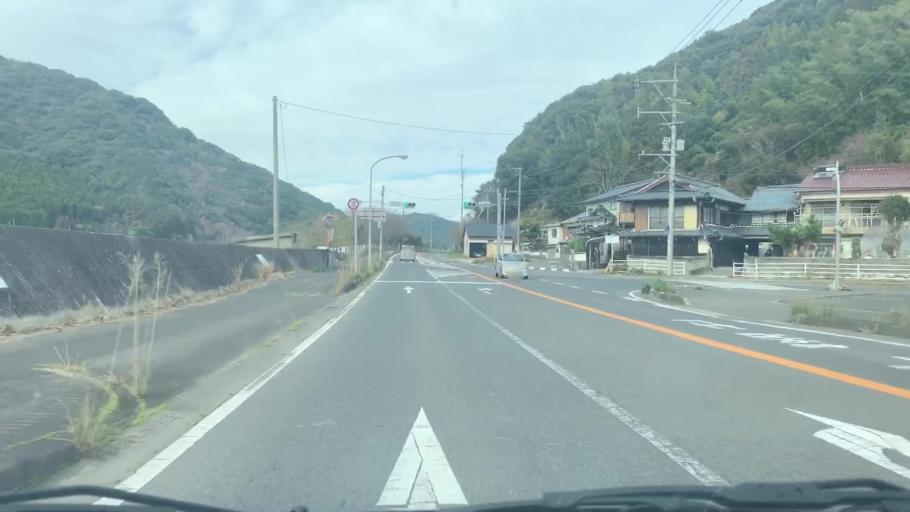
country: JP
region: Saga Prefecture
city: Karatsu
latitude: 33.3635
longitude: 130.0090
